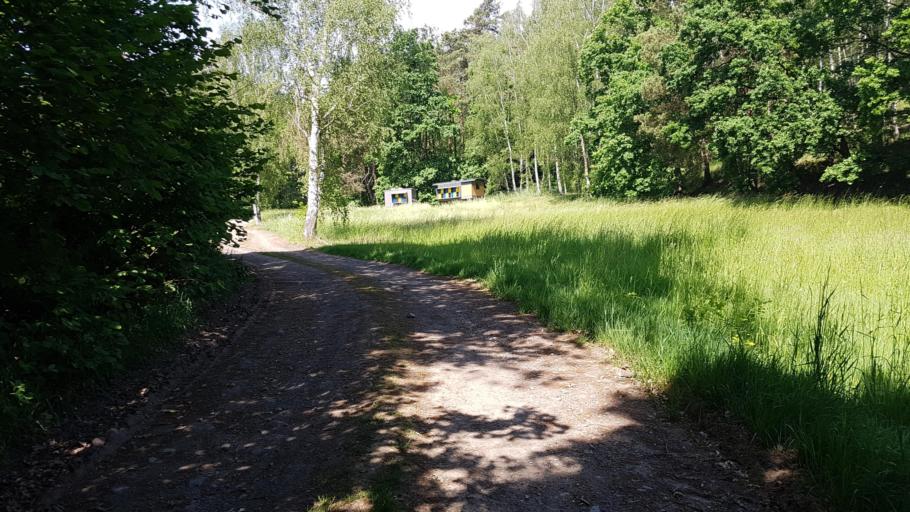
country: DE
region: Brandenburg
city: Grosskmehlen
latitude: 51.3648
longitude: 13.7084
